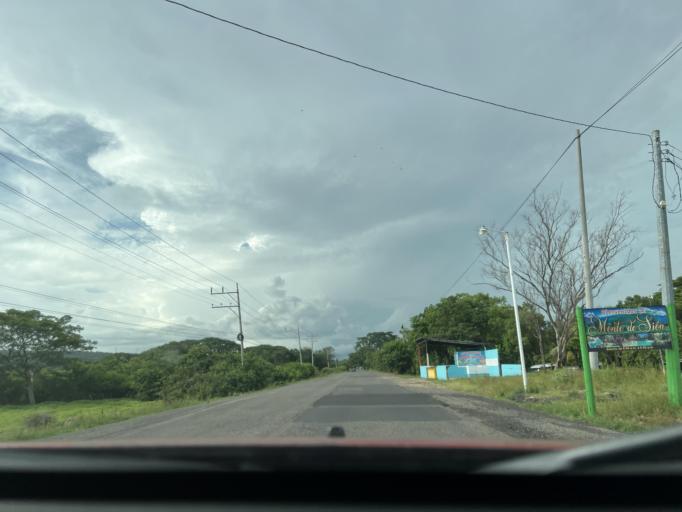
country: SV
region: La Union
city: San Alejo
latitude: 13.3808
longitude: -87.9067
